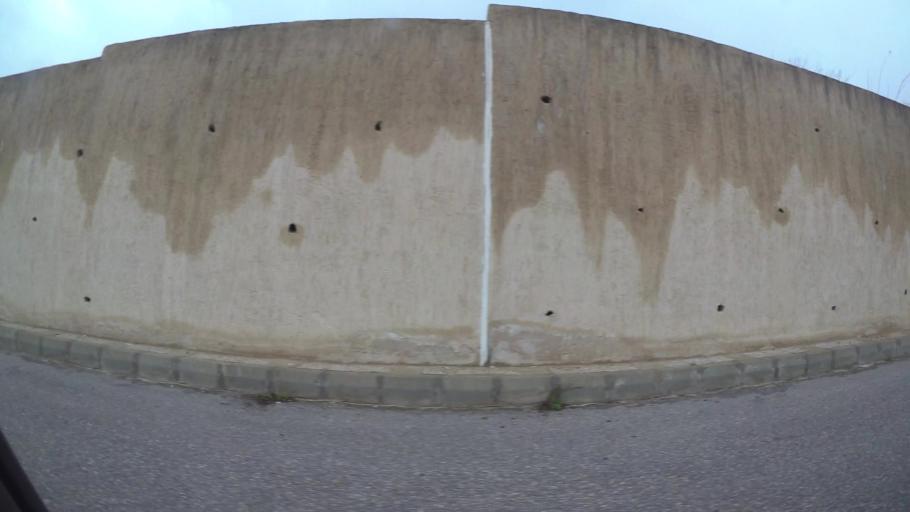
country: JO
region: Amman
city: Al Jubayhah
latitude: 32.0067
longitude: 35.8215
